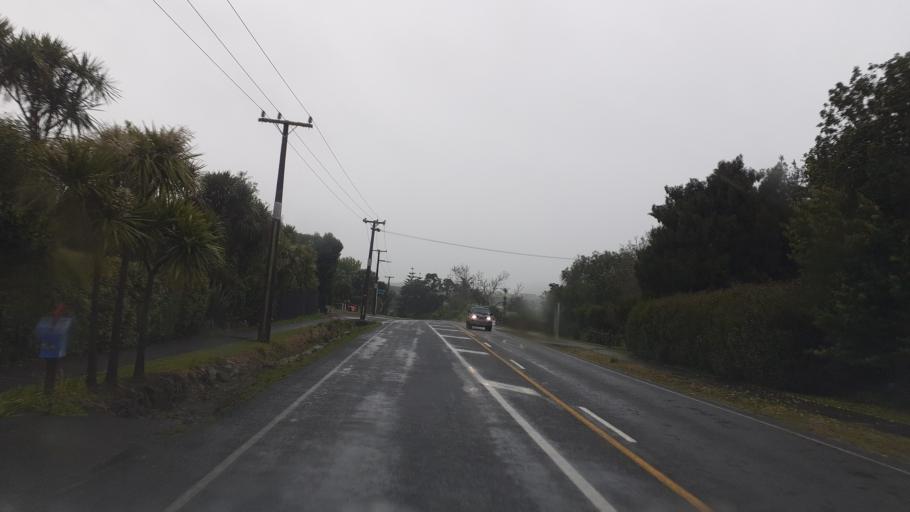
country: NZ
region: Northland
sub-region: Far North District
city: Kerikeri
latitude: -35.2072
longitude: 173.9647
